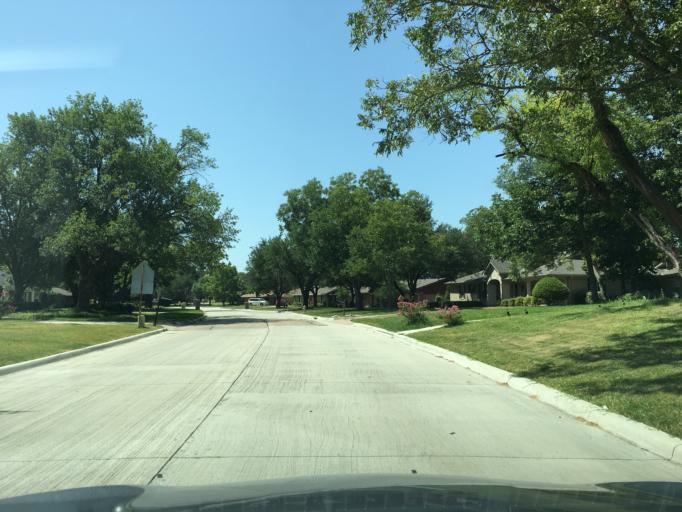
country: US
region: Texas
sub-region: Dallas County
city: Garland
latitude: 32.8767
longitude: -96.6057
